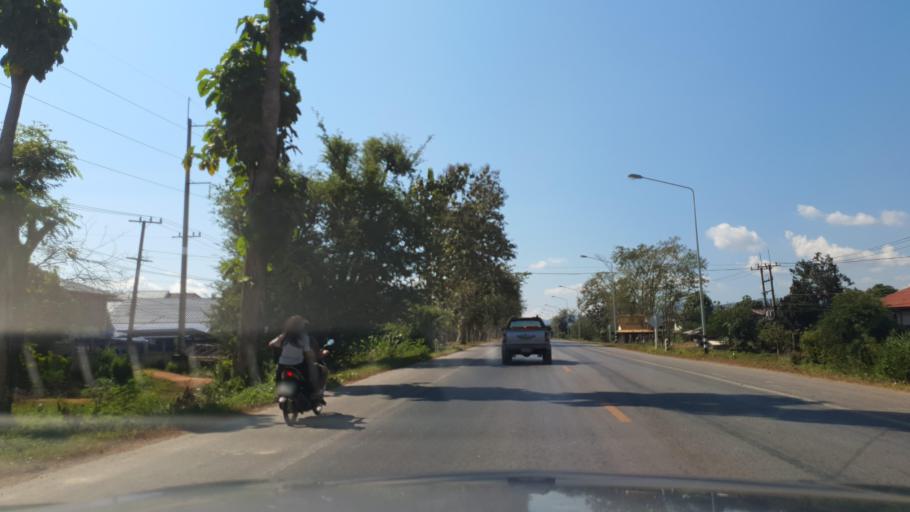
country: TH
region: Nan
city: Tha Wang Pha
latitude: 19.0213
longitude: 100.7914
